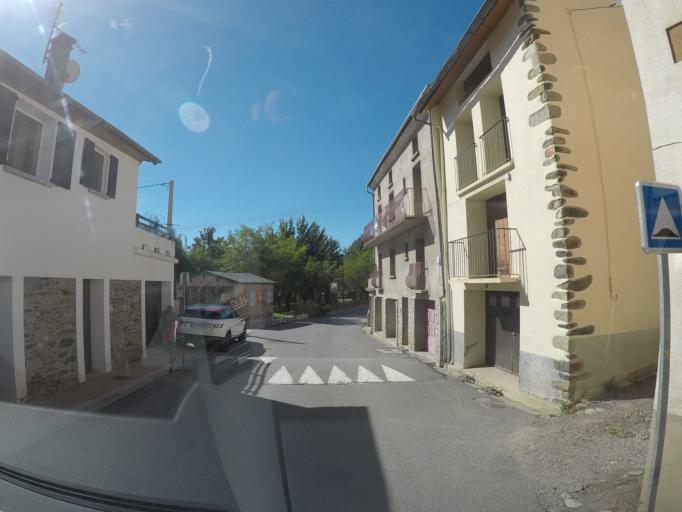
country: ES
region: Catalonia
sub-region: Provincia de Girona
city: Llivia
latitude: 42.4677
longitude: 1.9967
